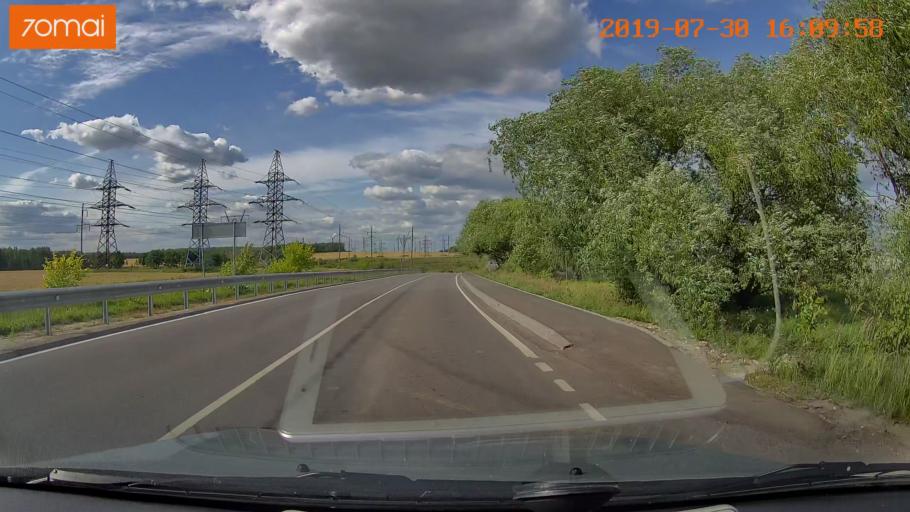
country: RU
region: Moskovskaya
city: Peski
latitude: 55.2579
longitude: 38.7156
